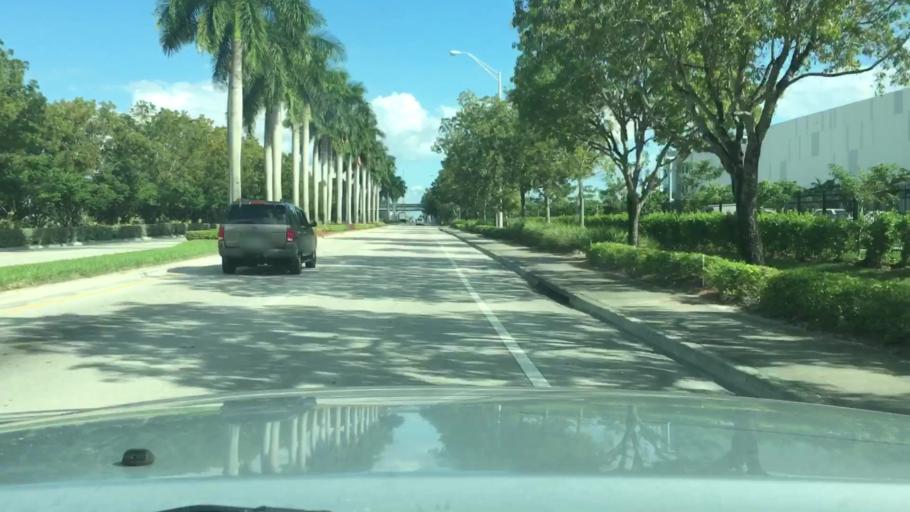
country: US
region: Florida
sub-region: Miami-Dade County
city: Sweetwater
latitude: 25.7967
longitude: -80.3899
